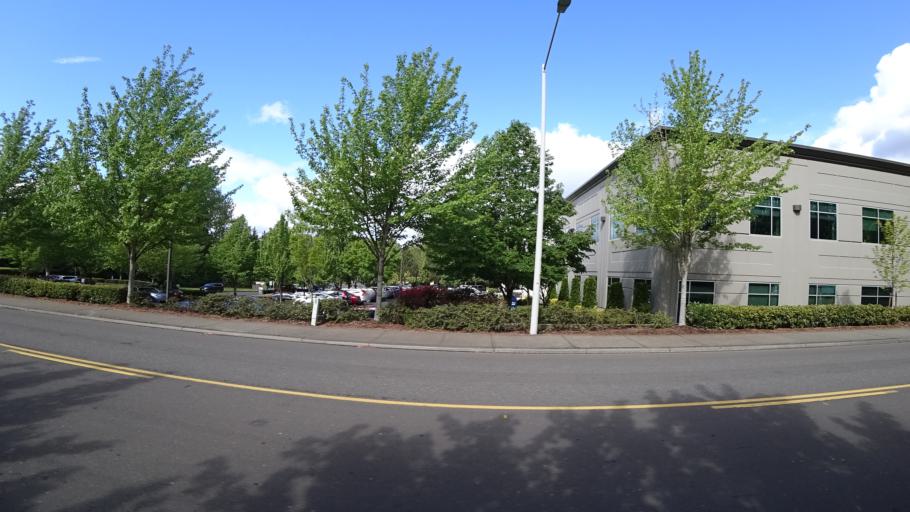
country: US
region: Oregon
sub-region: Washington County
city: Durham
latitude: 45.4220
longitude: -122.7518
